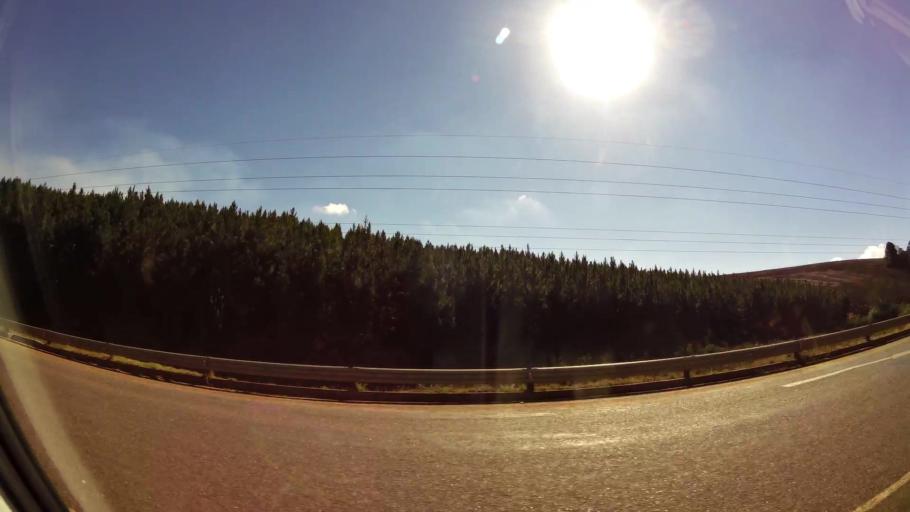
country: ZA
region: Limpopo
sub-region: Capricorn District Municipality
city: Mankoeng
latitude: -23.9375
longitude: 29.9517
